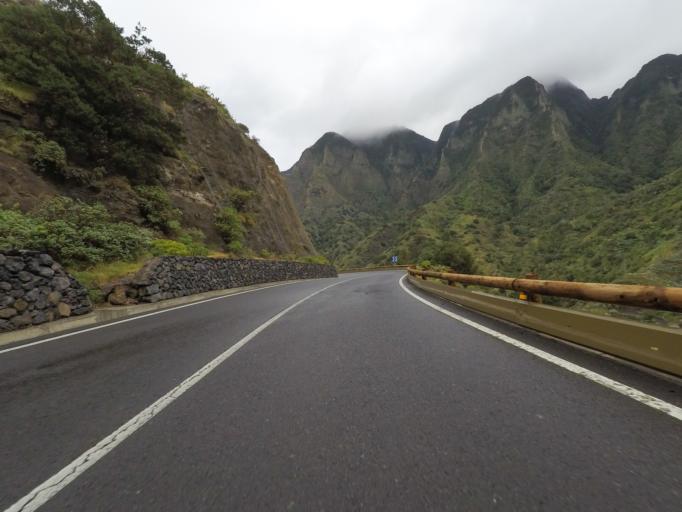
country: ES
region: Canary Islands
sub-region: Provincia de Santa Cruz de Tenerife
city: Hermigua
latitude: 28.1406
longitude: -17.1973
